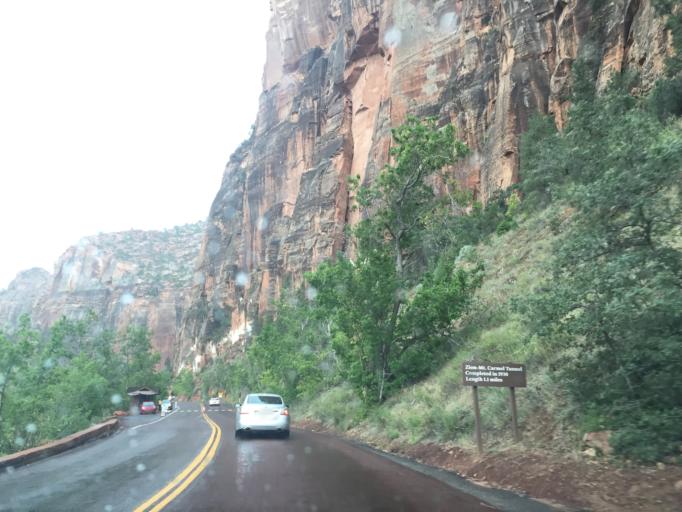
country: US
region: Utah
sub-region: Washington County
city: Hildale
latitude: 37.2122
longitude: -112.9612
